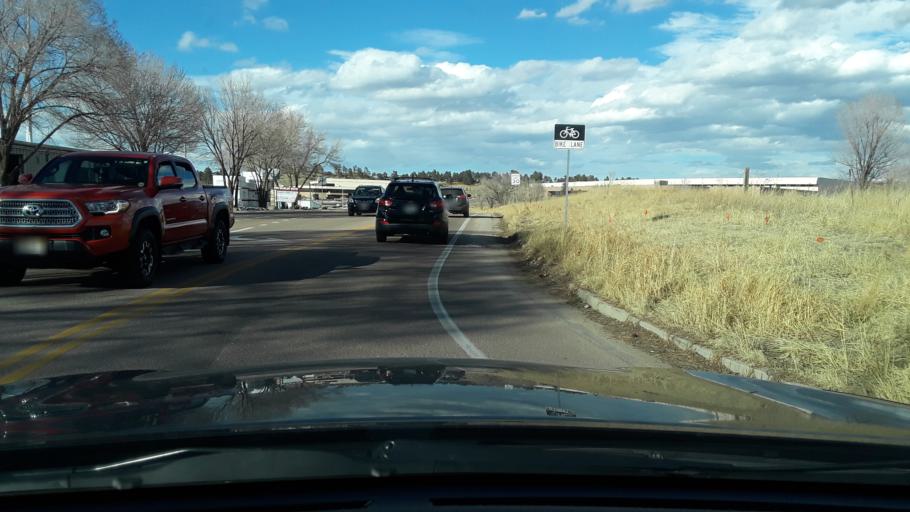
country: US
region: Colorado
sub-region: El Paso County
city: Air Force Academy
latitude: 38.9259
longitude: -104.8103
